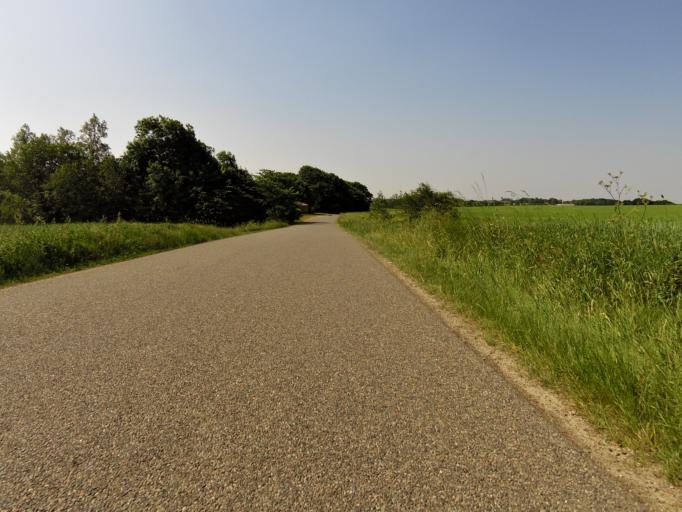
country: DK
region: Central Jutland
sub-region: Holstebro Kommune
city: Vinderup
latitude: 56.4793
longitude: 8.8282
